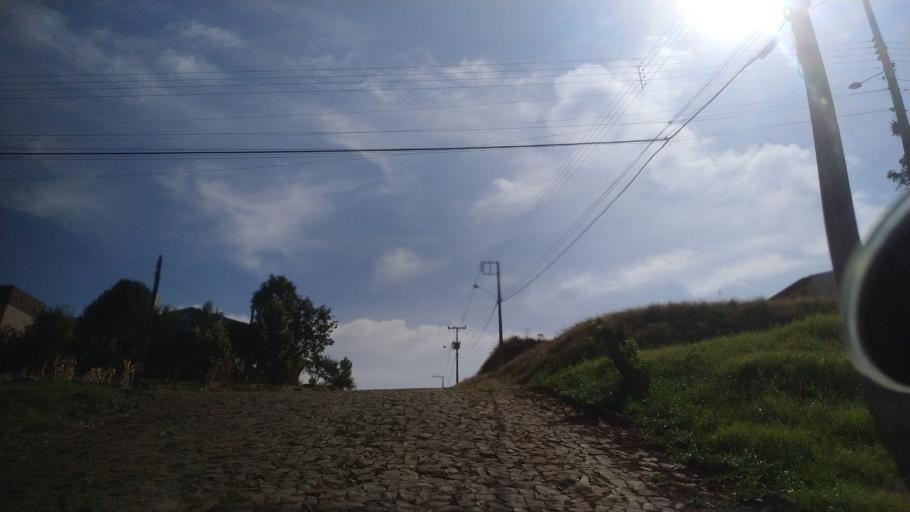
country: BR
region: Santa Catarina
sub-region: Chapeco
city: Chapeco
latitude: -27.1107
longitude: -52.5975
